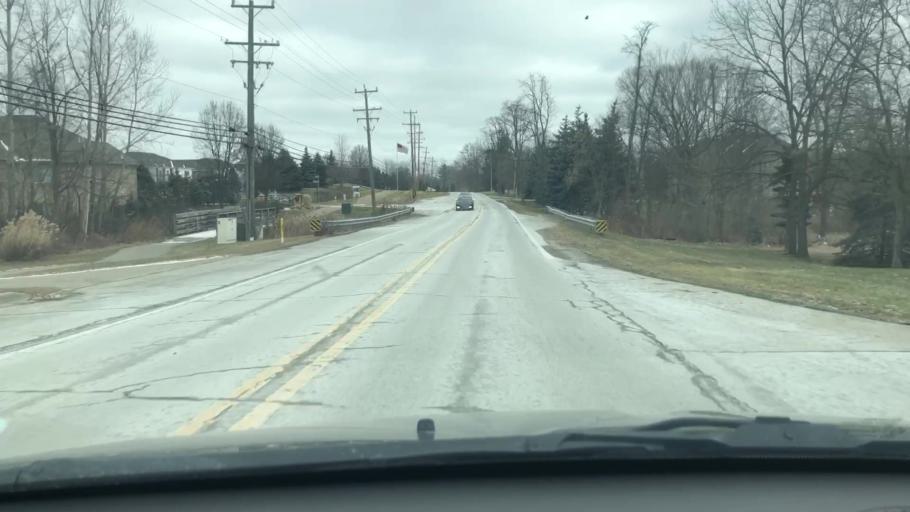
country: US
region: Michigan
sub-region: Macomb County
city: Shelby
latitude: 42.7238
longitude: -83.0502
